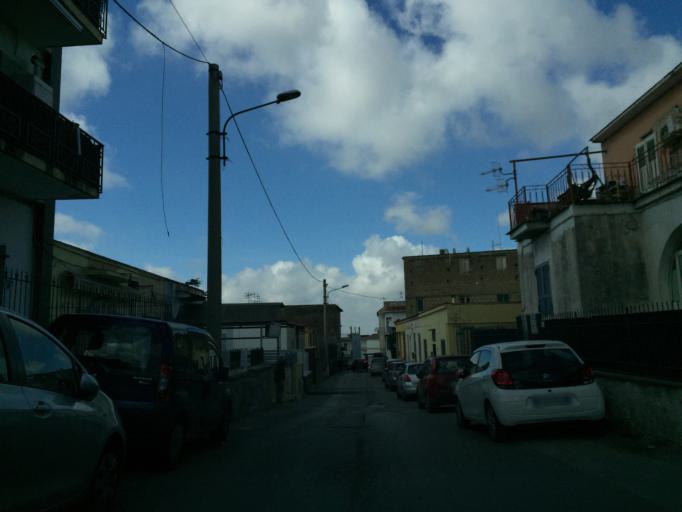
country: IT
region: Campania
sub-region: Provincia di Napoli
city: Massa di Somma
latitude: 40.8448
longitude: 14.3738
